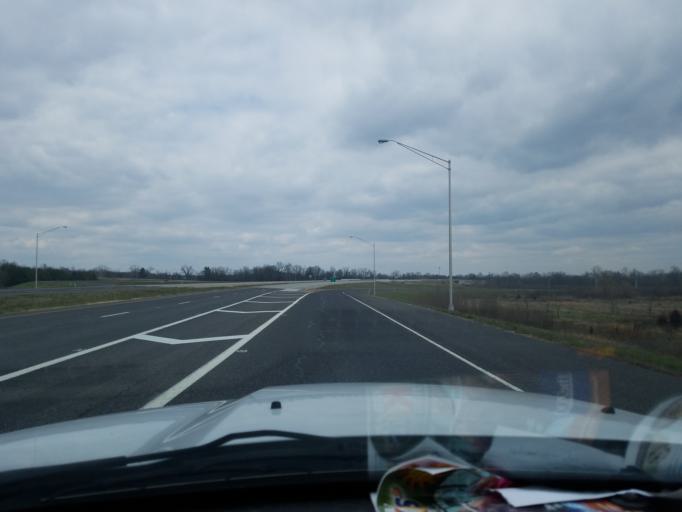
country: US
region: Indiana
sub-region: Vigo County
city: Terre Haute
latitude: 39.3937
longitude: -87.3728
